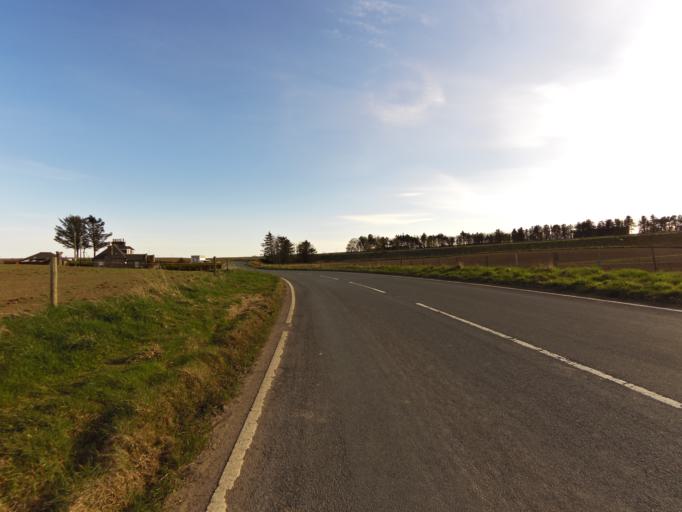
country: GB
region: Scotland
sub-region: Aberdeenshire
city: Stonehaven
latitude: 56.9439
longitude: -2.2075
